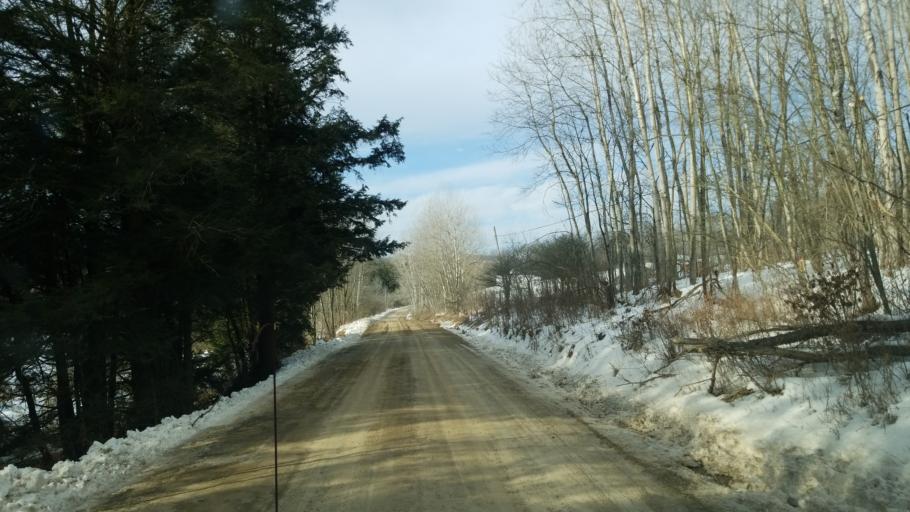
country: US
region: New York
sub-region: Allegany County
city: Andover
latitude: 41.9534
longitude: -77.7528
